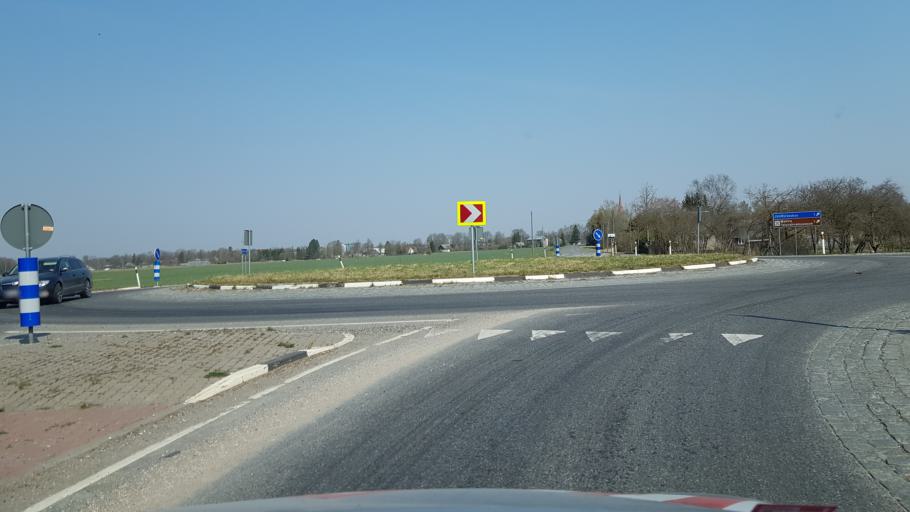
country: EE
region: Raplamaa
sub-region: Kehtna vald
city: Kehtna
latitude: 59.0552
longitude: 24.9504
